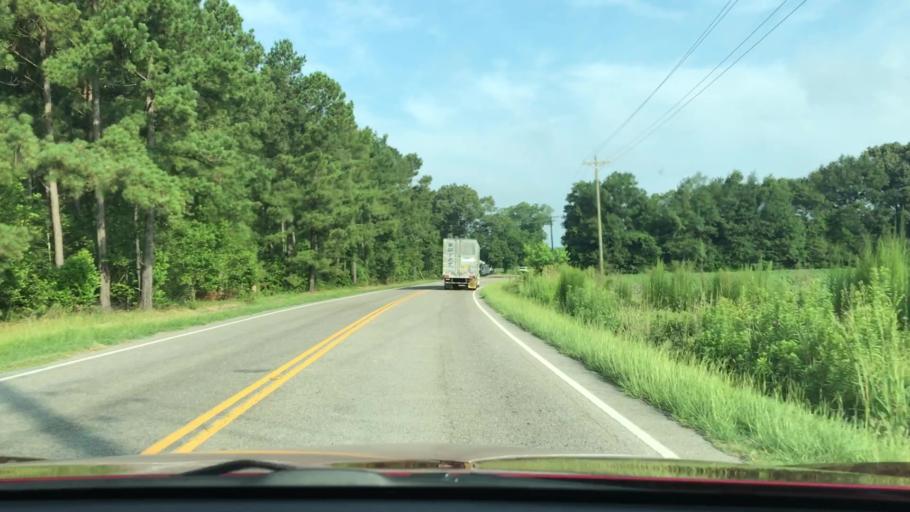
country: US
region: South Carolina
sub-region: Barnwell County
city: Blackville
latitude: 33.5962
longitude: -81.2566
